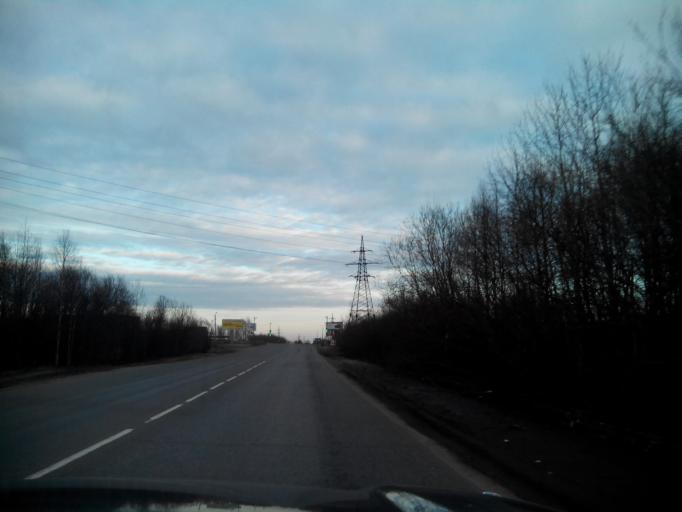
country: RU
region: Arkhangelskaya
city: Arkhangel'sk
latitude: 64.5206
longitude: 40.6736
